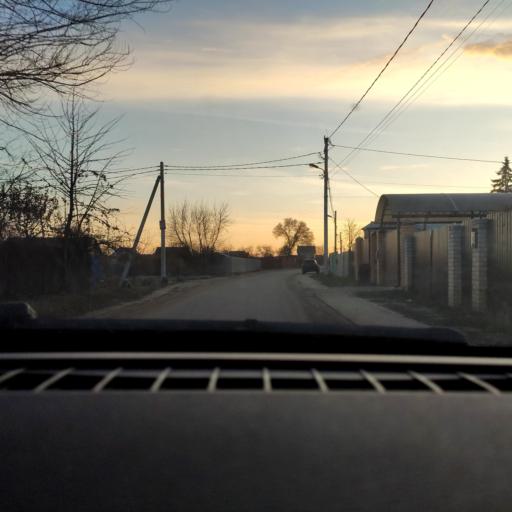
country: RU
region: Voronezj
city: Maslovka
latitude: 51.6155
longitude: 39.2626
